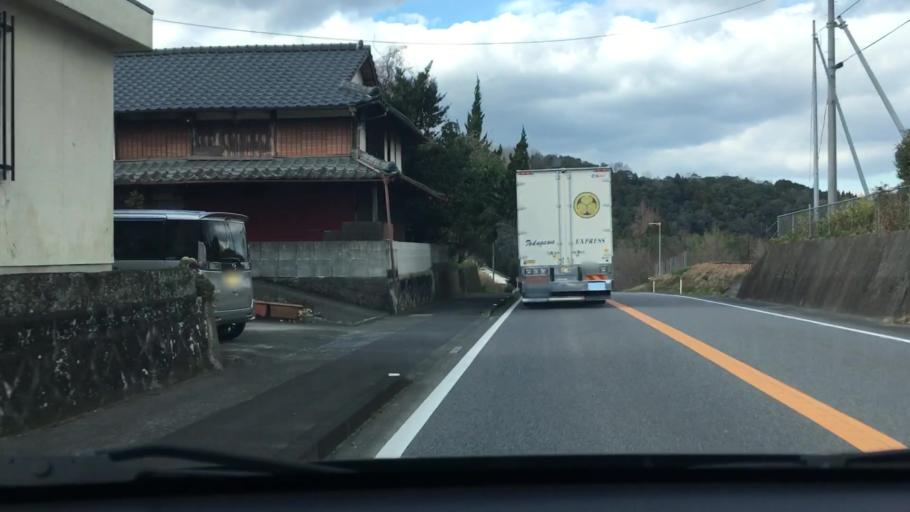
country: JP
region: Oita
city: Usuki
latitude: 33.0207
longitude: 131.6974
